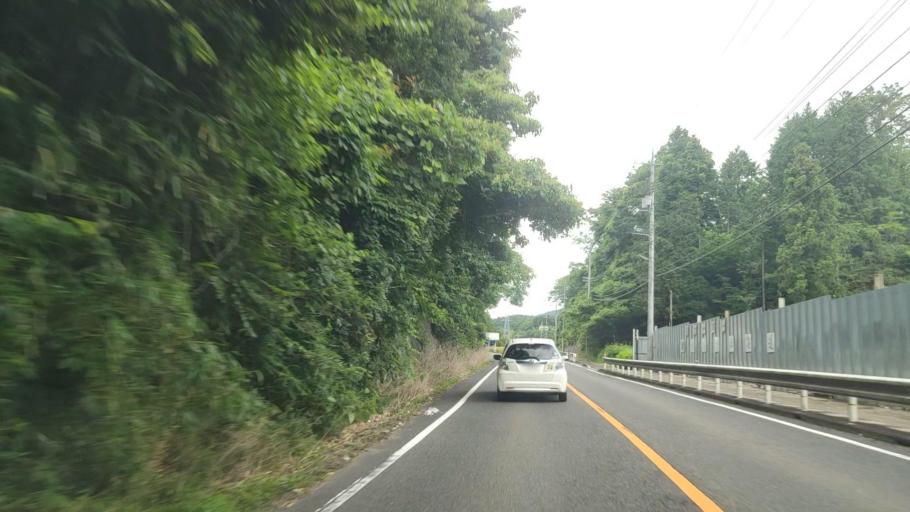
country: JP
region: Okayama
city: Tsuyama
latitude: 35.0602
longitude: 133.8585
